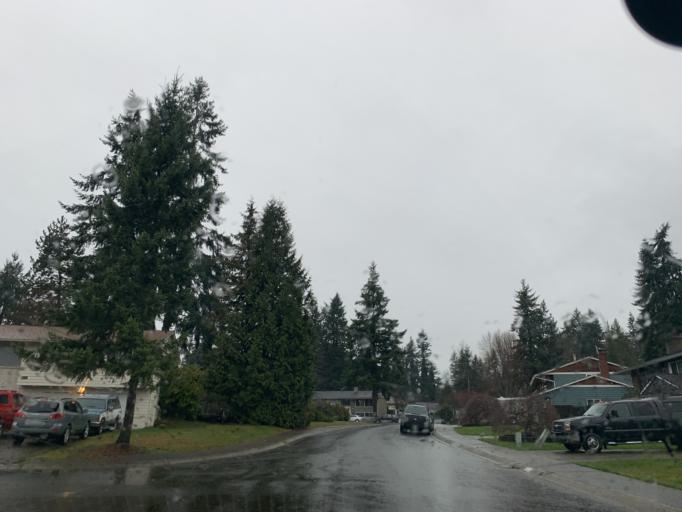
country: US
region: Washington
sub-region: King County
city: Kingsgate
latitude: 47.7377
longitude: -122.1848
